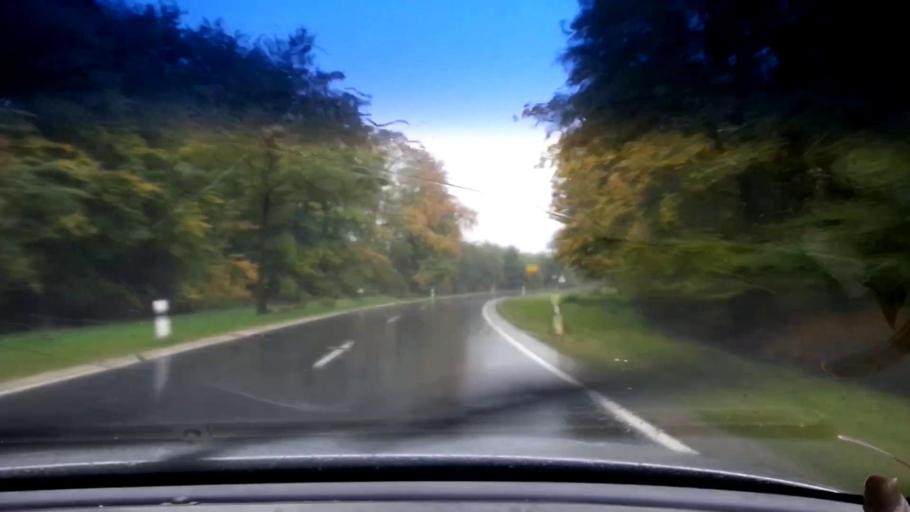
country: DE
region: Bavaria
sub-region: Upper Franconia
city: Wattendorf
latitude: 50.0210
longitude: 11.0888
